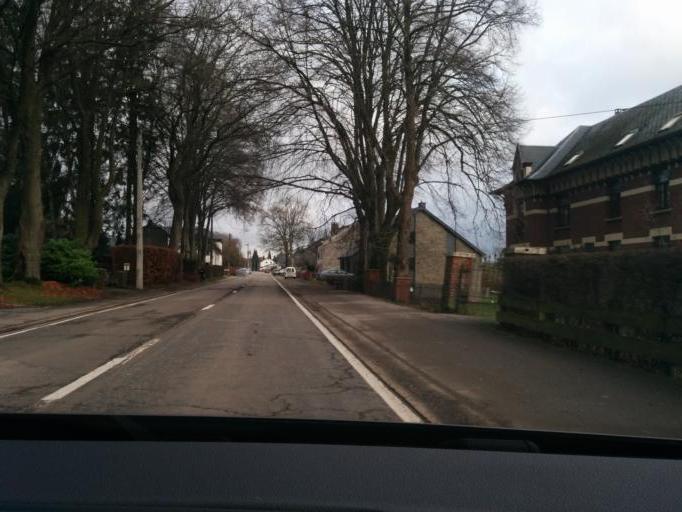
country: BE
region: Wallonia
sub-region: Province du Luxembourg
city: Gouvy
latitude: 50.1862
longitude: 5.9450
